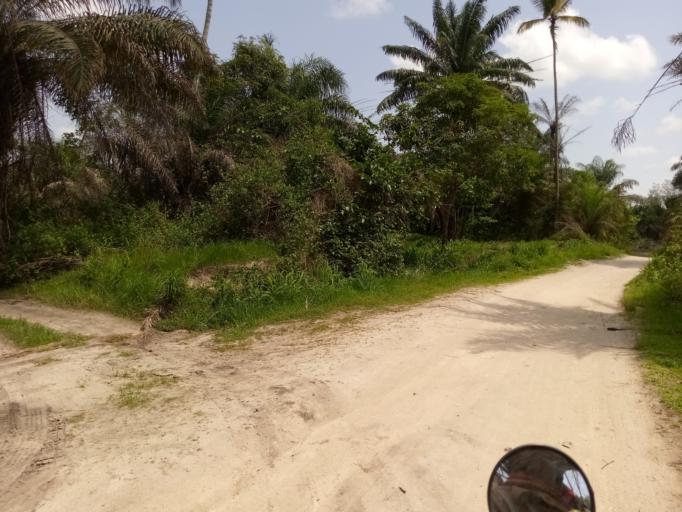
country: SL
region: Western Area
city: Waterloo
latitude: 8.3660
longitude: -13.0024
